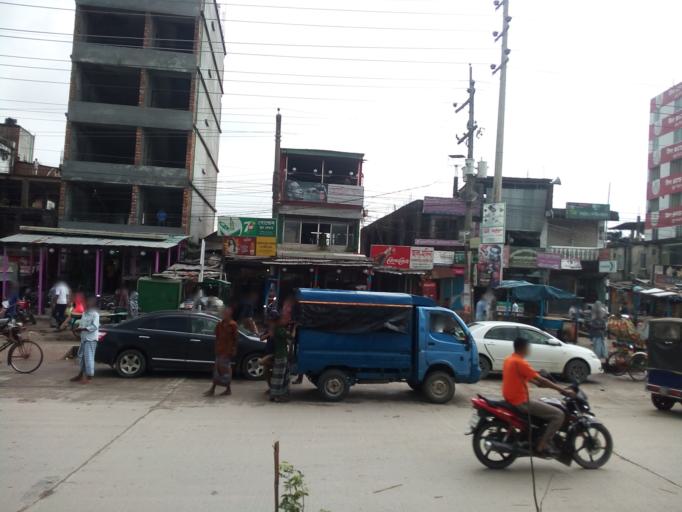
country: BD
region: Dhaka
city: Gafargaon
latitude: 24.4053
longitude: 90.3856
